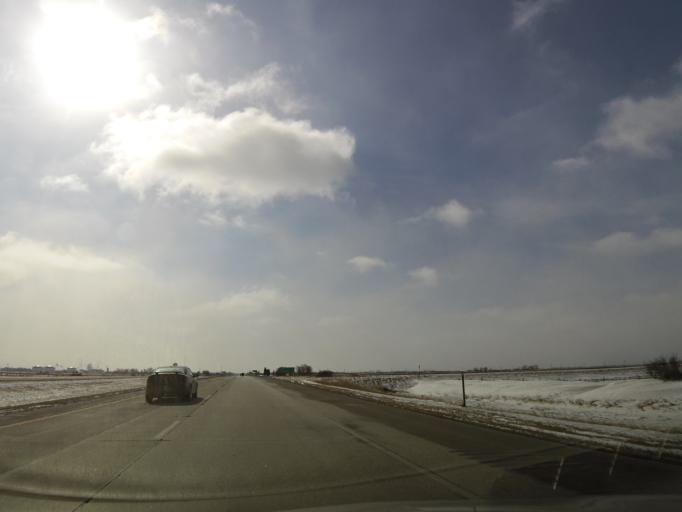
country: US
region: North Dakota
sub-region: Grand Forks County
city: Grand Forks
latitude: 47.9634
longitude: -97.0935
